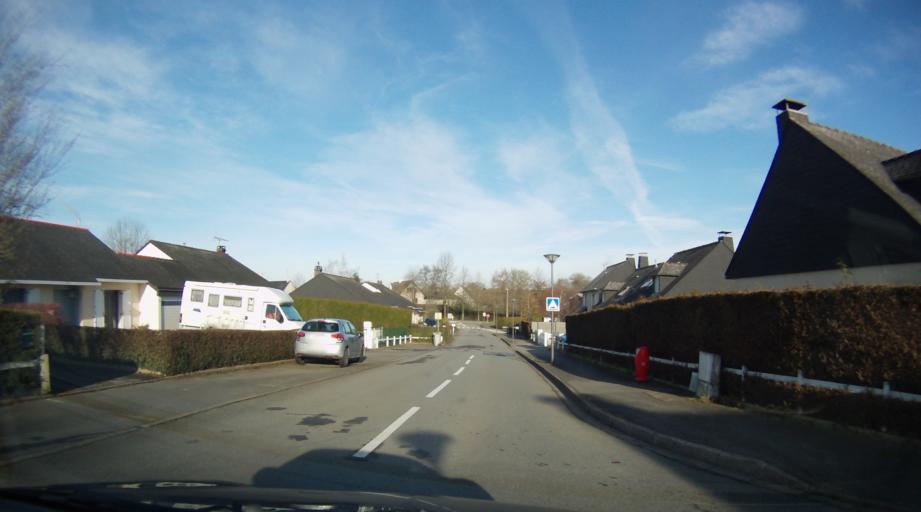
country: FR
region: Brittany
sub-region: Departement d'Ille-et-Vilaine
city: Bourgbarre
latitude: 47.9964
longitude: -1.6125
